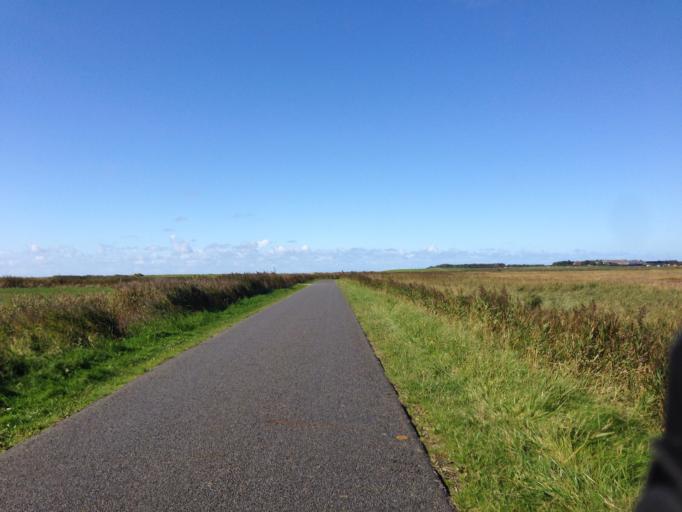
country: DE
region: Schleswig-Holstein
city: Witsum
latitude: 54.6964
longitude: 8.4307
